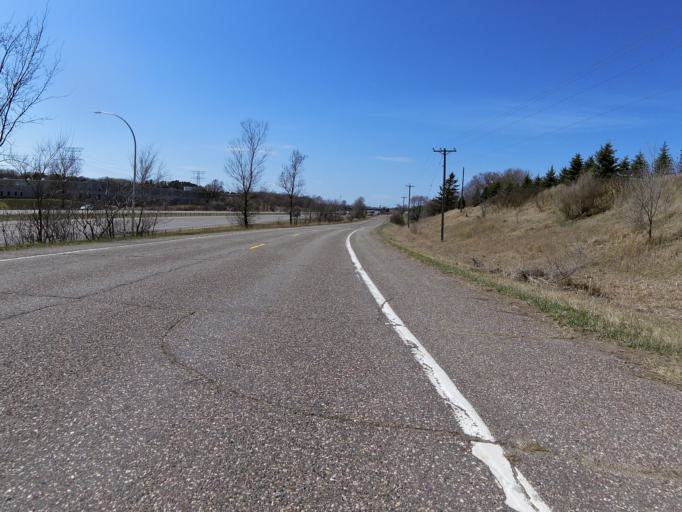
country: US
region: Minnesota
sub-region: Washington County
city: Lakeland
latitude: 44.9492
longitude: -92.8277
